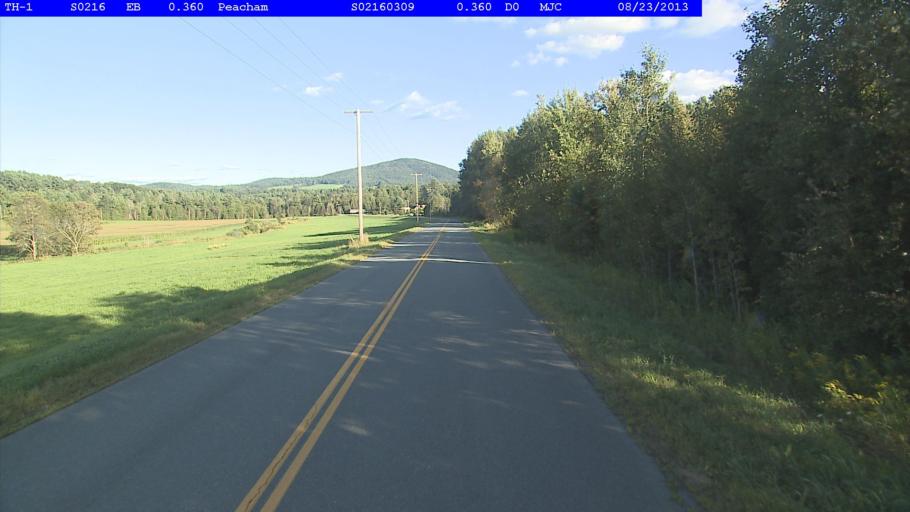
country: US
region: Vermont
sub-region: Caledonia County
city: Saint Johnsbury
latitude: 44.3125
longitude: -72.1600
